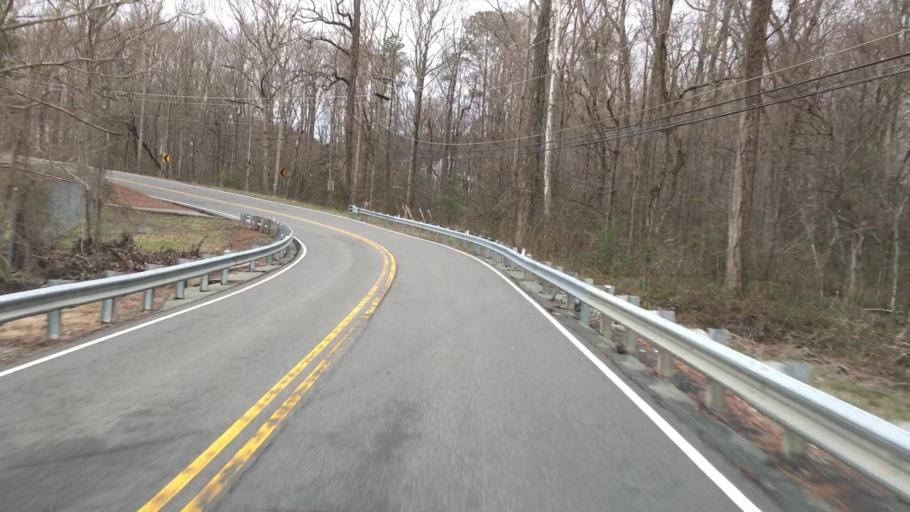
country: US
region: Virginia
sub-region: Henrico County
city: Glen Allen
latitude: 37.6750
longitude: -77.5479
